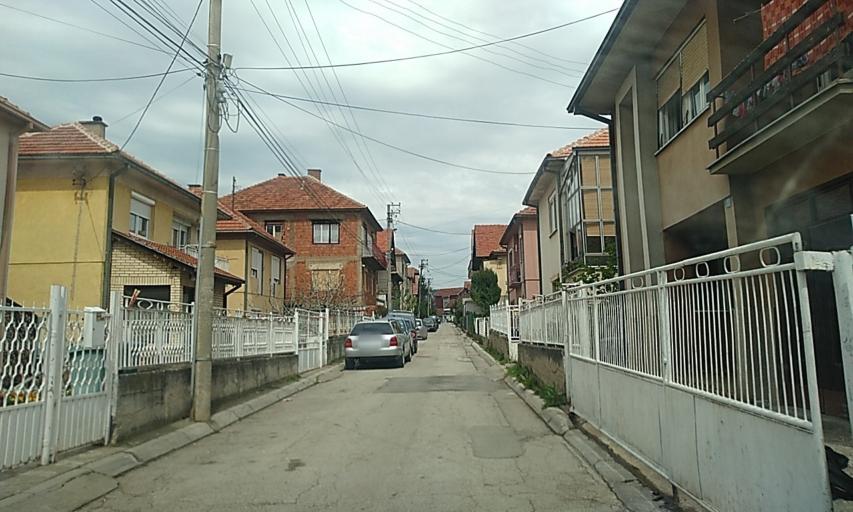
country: RS
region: Central Serbia
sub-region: Nisavski Okrug
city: Nis
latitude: 43.3352
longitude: 21.9152
